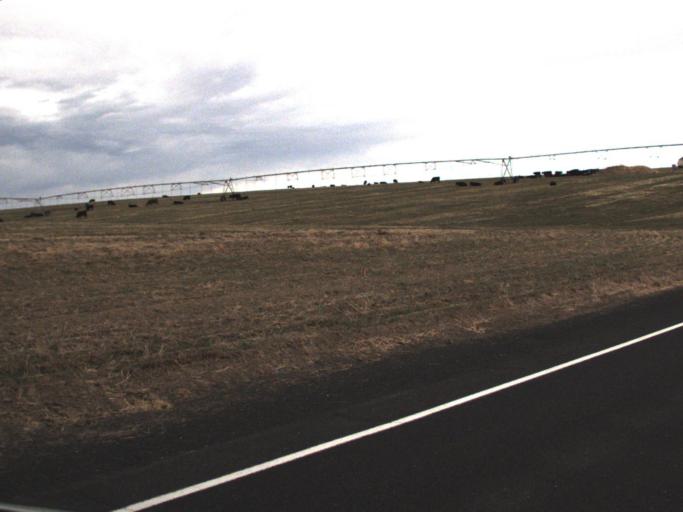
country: US
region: Washington
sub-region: Okanogan County
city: Coulee Dam
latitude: 47.6125
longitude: -118.7600
